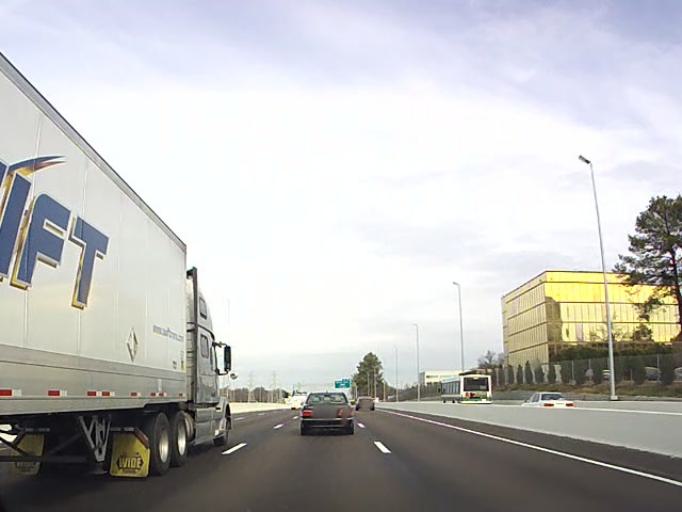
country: US
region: Tennessee
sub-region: Shelby County
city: Germantown
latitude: 35.1084
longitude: -89.8699
